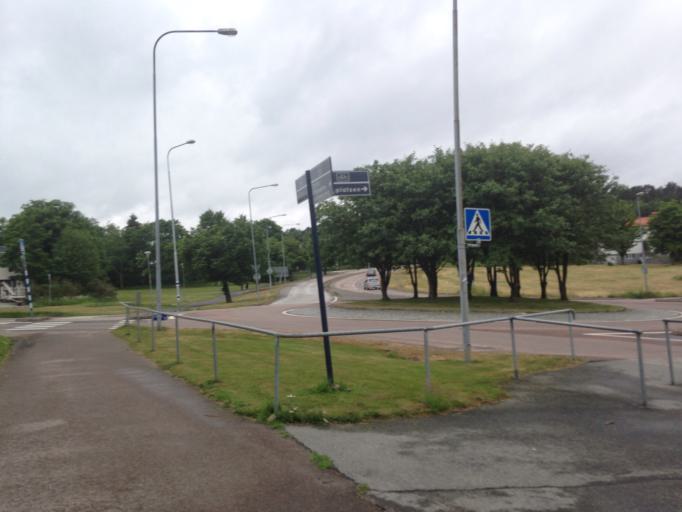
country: SE
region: Vaestra Goetaland
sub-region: Partille Kommun
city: Partille
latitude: 57.7192
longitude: 12.0679
